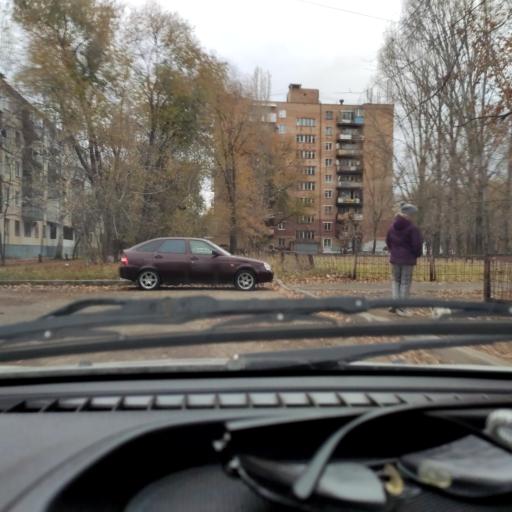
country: RU
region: Samara
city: Tol'yatti
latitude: 53.5017
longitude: 49.4060
